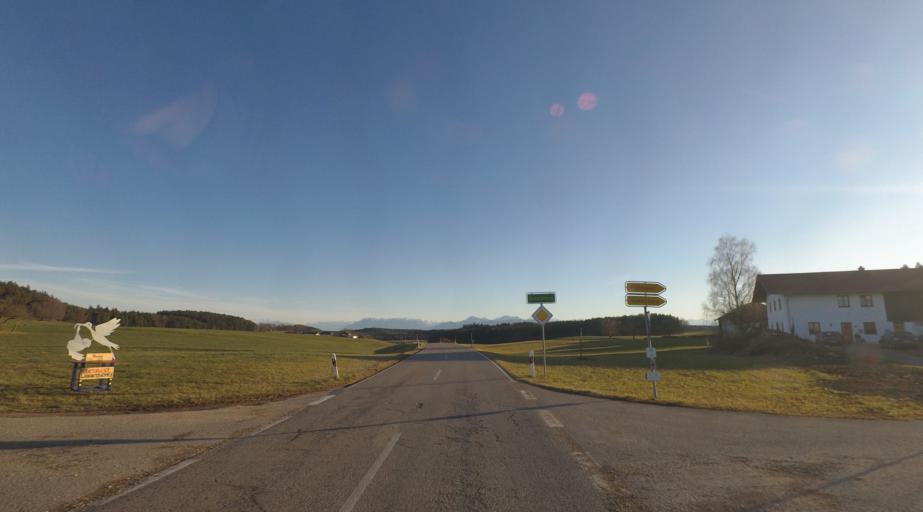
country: DE
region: Bavaria
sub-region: Upper Bavaria
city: Palling
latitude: 48.0044
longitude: 12.6916
